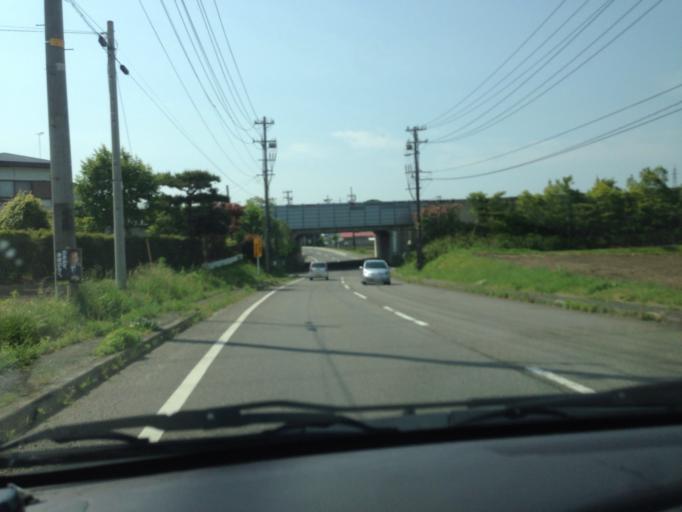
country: JP
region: Tochigi
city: Kuroiso
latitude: 37.1382
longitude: 140.1928
